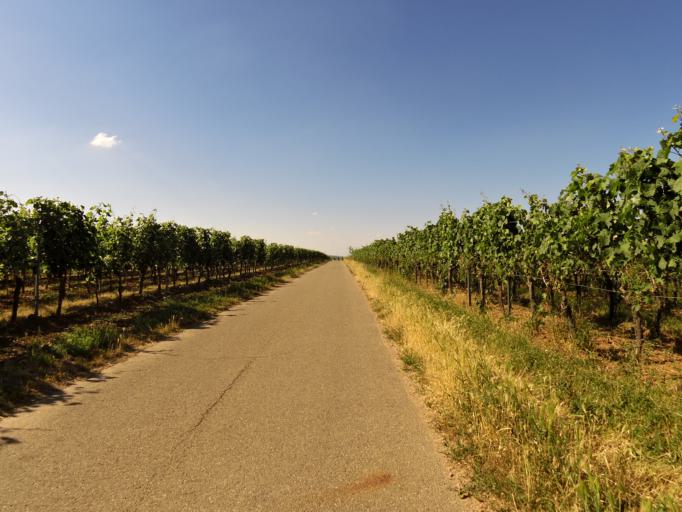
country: DE
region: Rheinland-Pfalz
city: Friedelsheim
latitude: 49.4592
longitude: 8.2066
